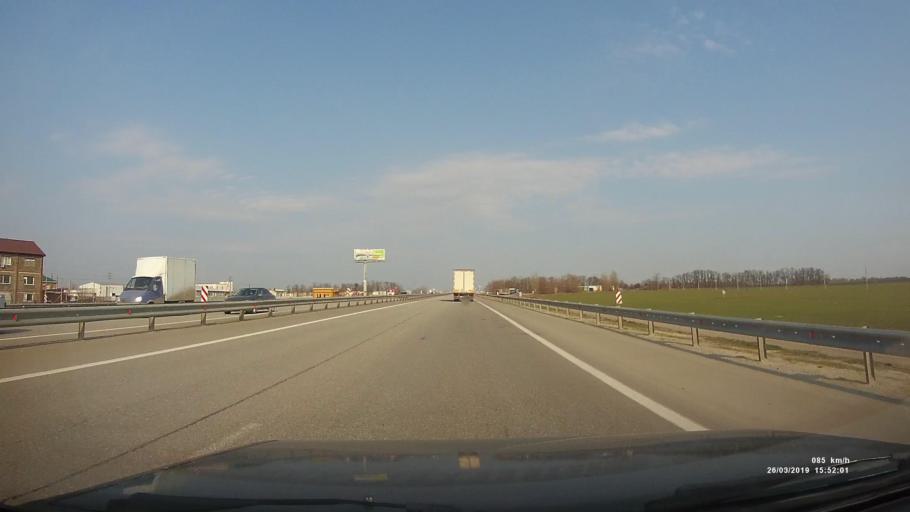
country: RU
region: Rostov
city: Kalinin
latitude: 47.2710
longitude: 39.5152
